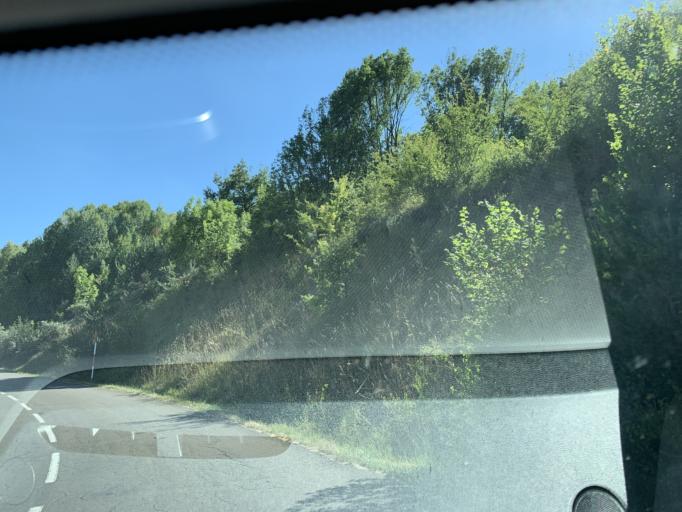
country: ES
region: Aragon
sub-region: Provincia de Huesca
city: Hoz de Jaca
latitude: 42.7038
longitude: -0.3243
